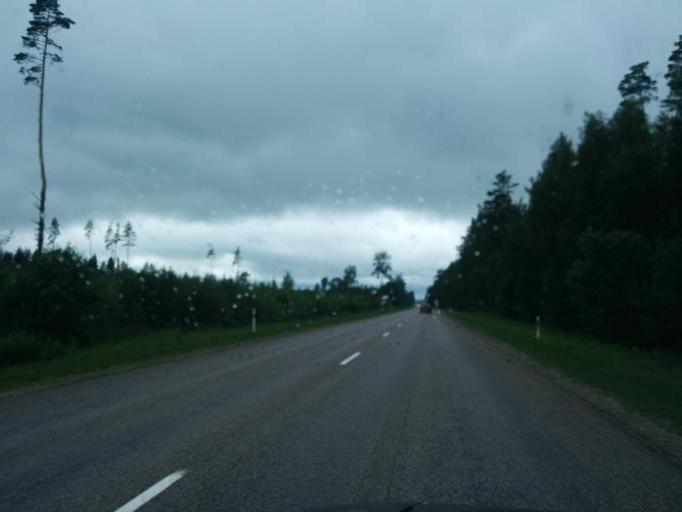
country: LV
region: Beverina
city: Murmuiza
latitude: 57.4878
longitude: 25.5873
